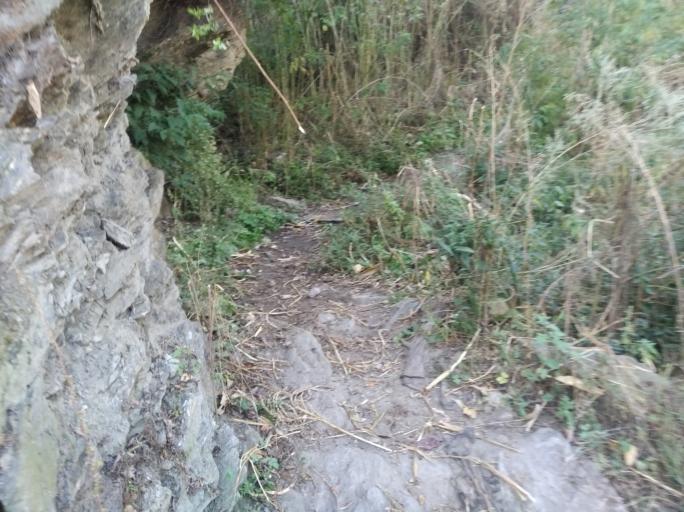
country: NP
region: Western Region
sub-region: Dhawalagiri Zone
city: Jomsom
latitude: 28.8806
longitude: 82.9825
